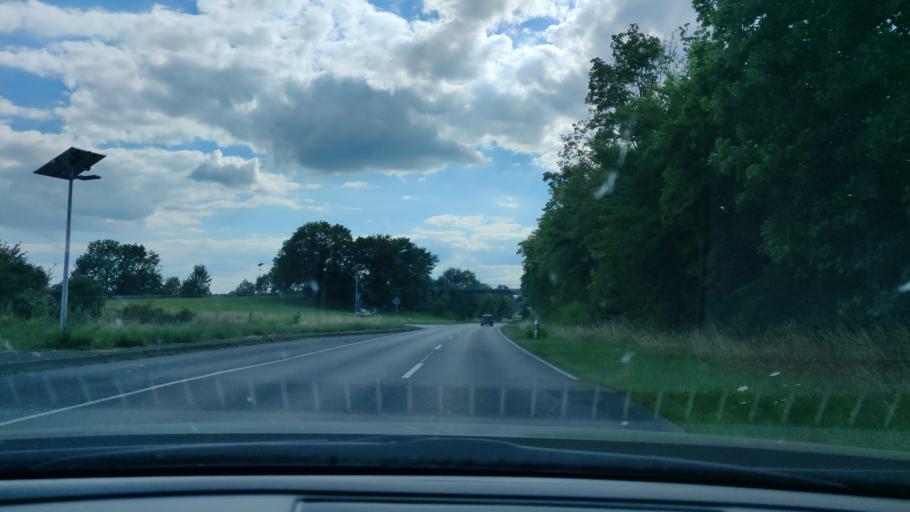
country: DE
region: Hesse
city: Gudensberg
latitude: 51.1661
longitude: 9.3210
